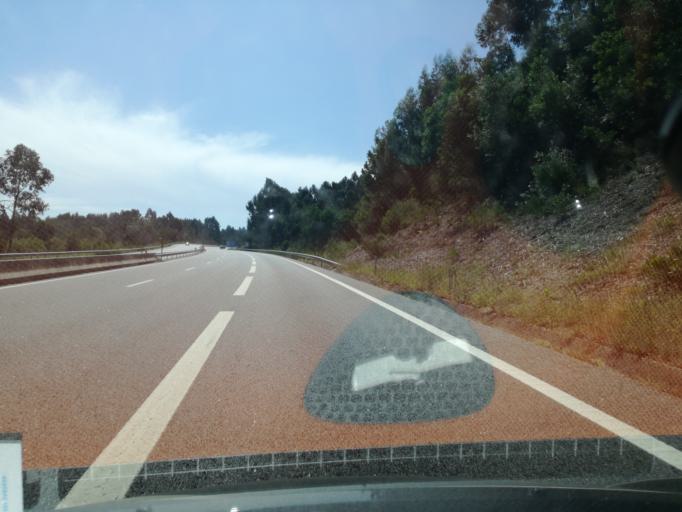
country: PT
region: Viana do Castelo
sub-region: Caminha
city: Vila Praia de Ancora
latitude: 41.7906
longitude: -8.7912
